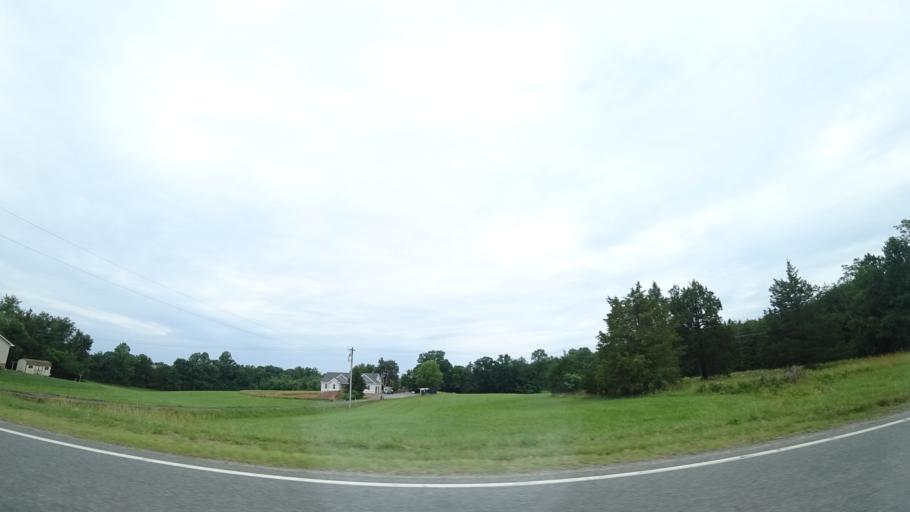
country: US
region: Virginia
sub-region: Spotsylvania County
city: Spotsylvania Courthouse
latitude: 38.1306
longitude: -77.7339
